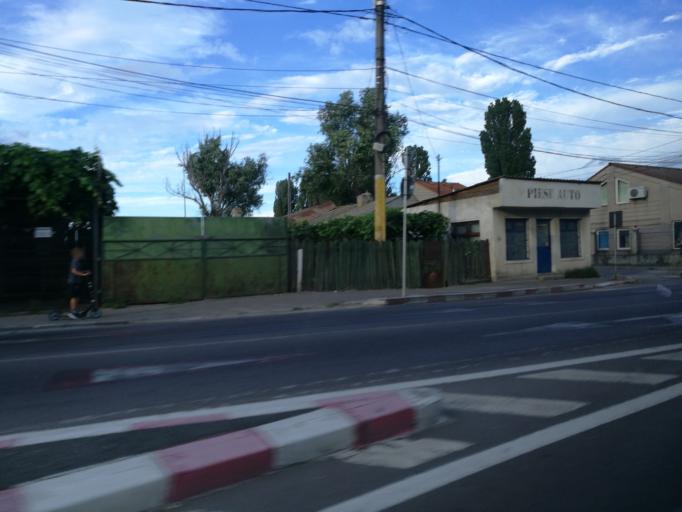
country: RO
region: Constanta
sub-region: Municipiul Constanta
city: Constanta
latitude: 44.1529
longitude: 28.6206
